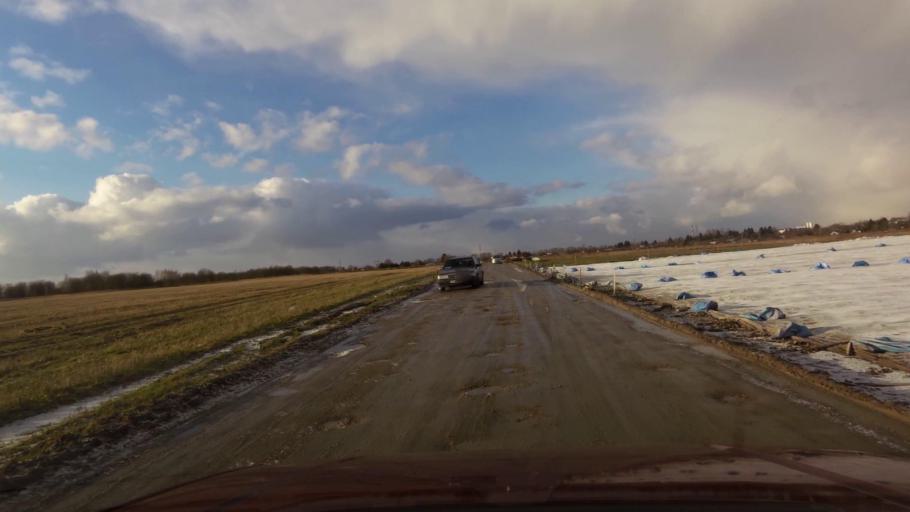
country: PL
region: West Pomeranian Voivodeship
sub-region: Koszalin
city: Koszalin
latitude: 54.1647
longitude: 16.1739
